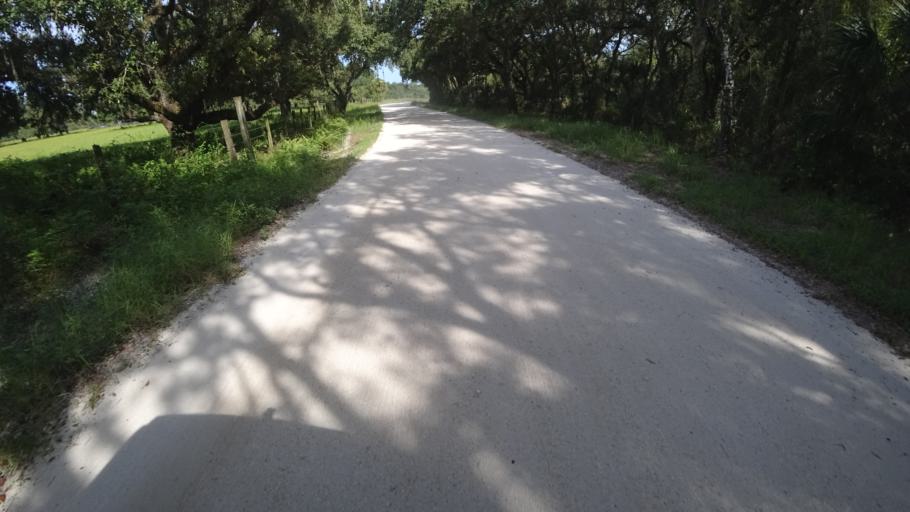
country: US
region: Florida
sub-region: Sarasota County
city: Lake Sarasota
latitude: 27.3141
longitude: -82.2201
